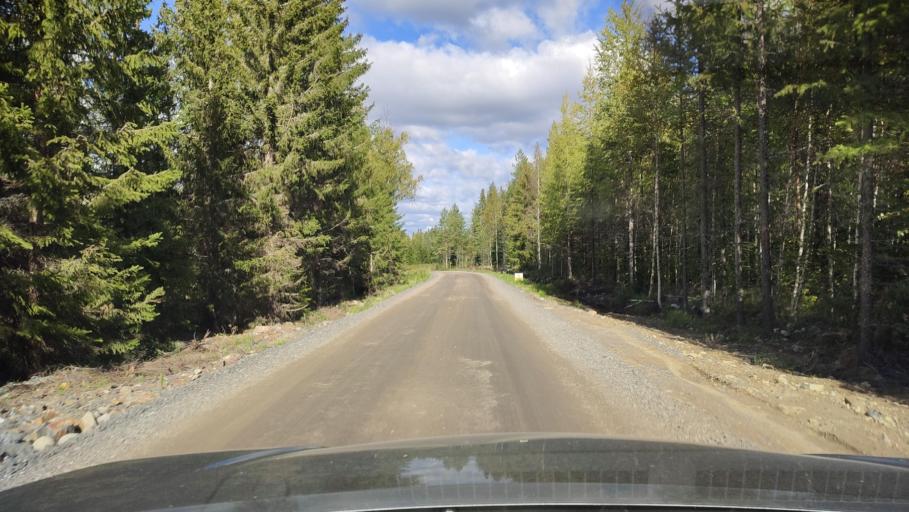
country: FI
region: Southern Ostrobothnia
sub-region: Suupohja
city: Karijoki
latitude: 62.1830
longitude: 21.5902
